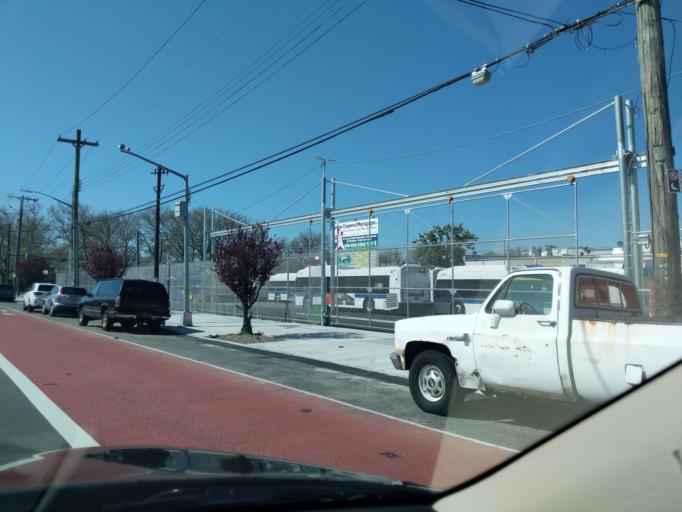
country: US
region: New York
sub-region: Kings County
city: Brooklyn
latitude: 40.6198
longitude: -73.9270
